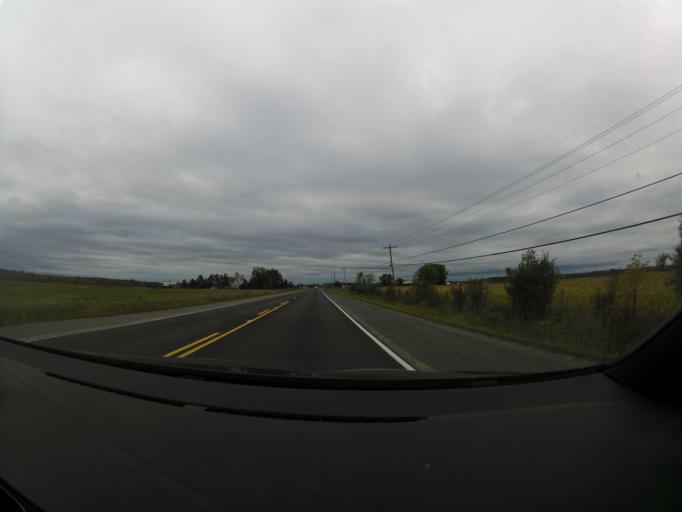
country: CA
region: Ontario
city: Bells Corners
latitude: 45.4311
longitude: -76.0325
